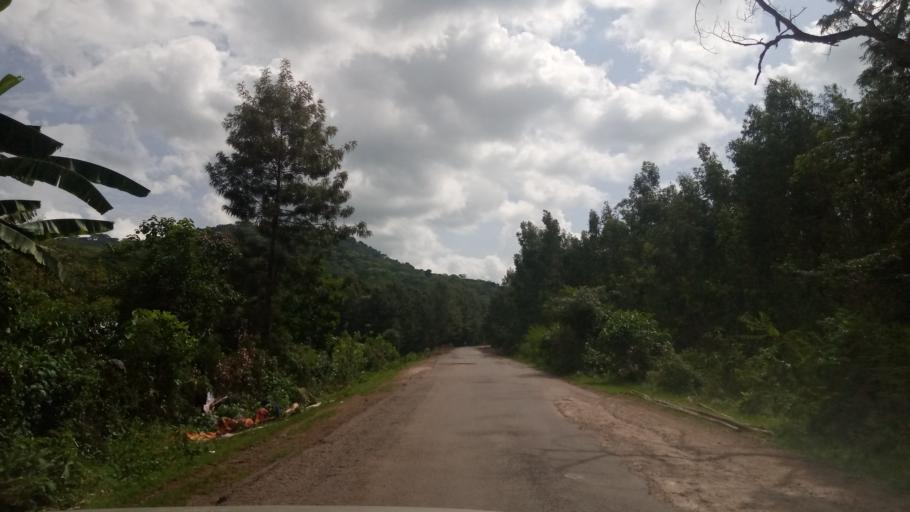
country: ET
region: Oromiya
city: Agaro
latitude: 7.9209
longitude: 36.5247
